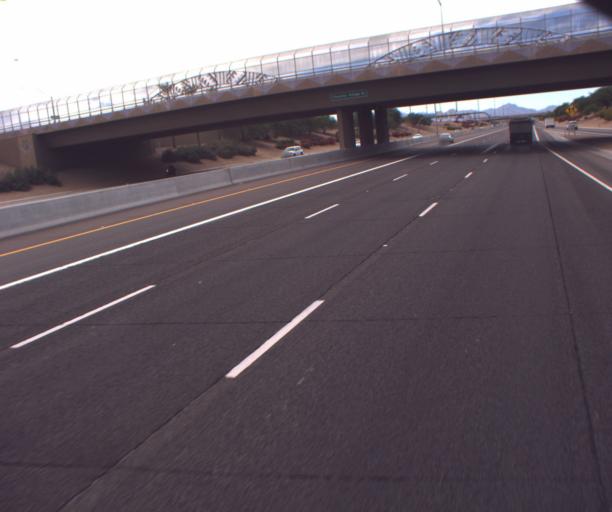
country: US
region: Arizona
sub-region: Maricopa County
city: Chandler
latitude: 33.2921
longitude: -111.9016
